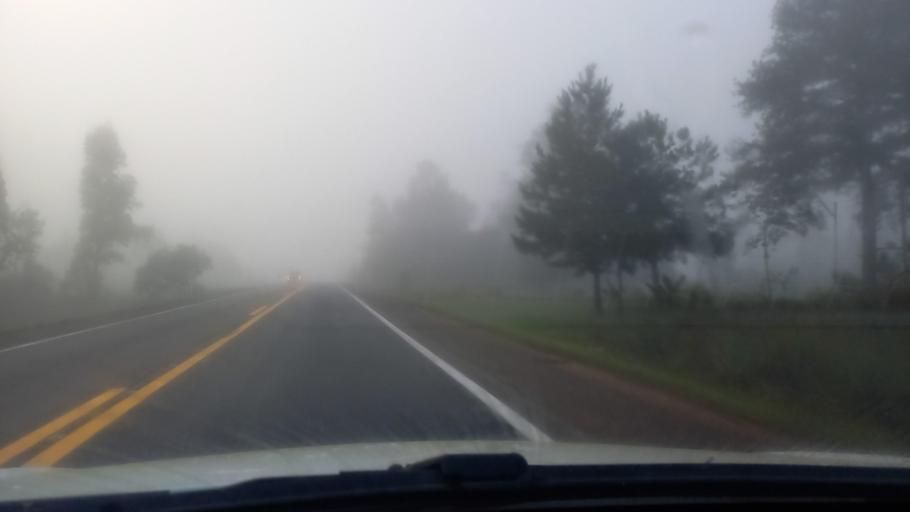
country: BR
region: Rio Grande do Sul
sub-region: Candelaria
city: Candelaria
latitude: -29.6902
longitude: -52.6888
